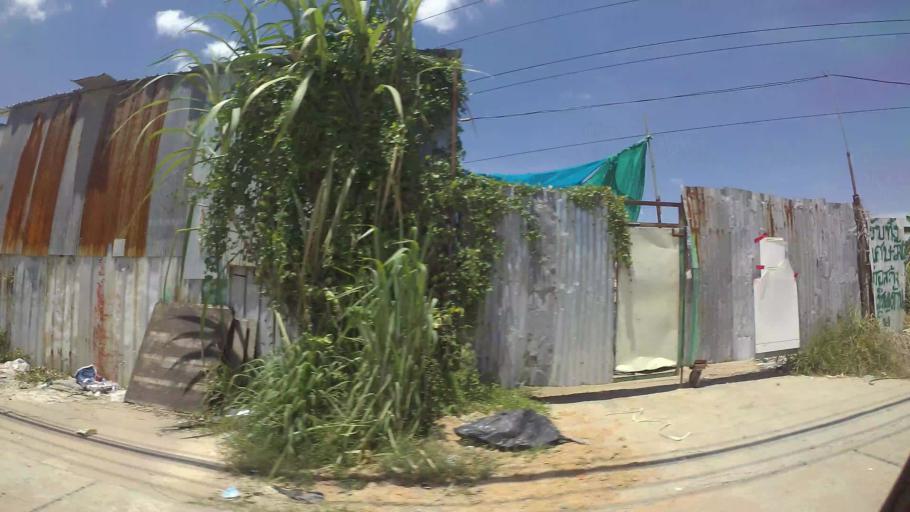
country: TH
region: Chon Buri
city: Si Racha
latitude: 13.1295
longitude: 100.9509
